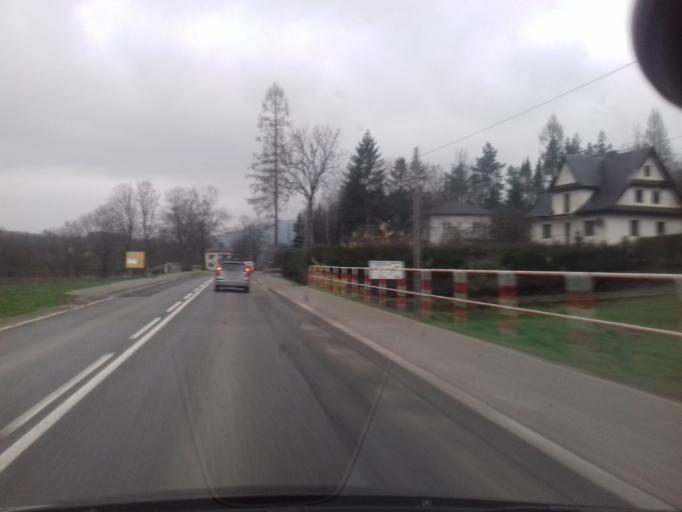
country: PL
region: Lesser Poland Voivodeship
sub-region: Powiat limanowski
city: Mszana Dolna
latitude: 49.6925
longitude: 20.0439
